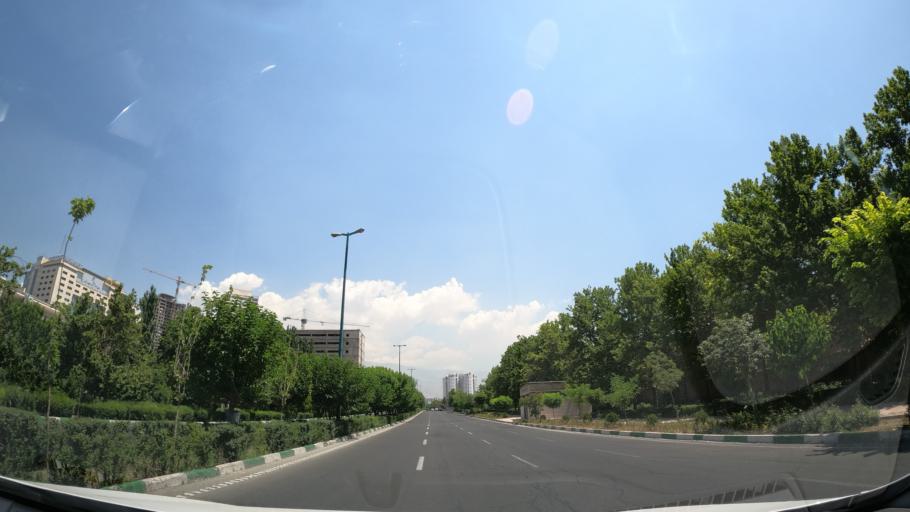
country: IR
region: Tehran
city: Tajrish
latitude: 35.7597
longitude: 51.3745
